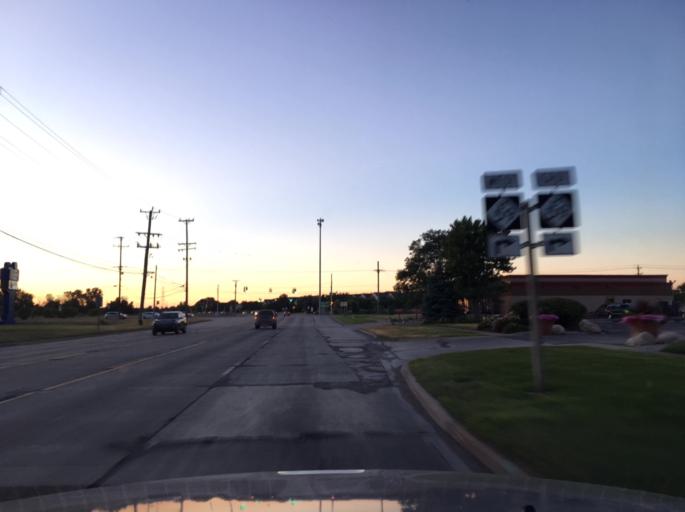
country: US
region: Michigan
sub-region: Macomb County
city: Clinton
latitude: 42.6263
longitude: -82.9533
